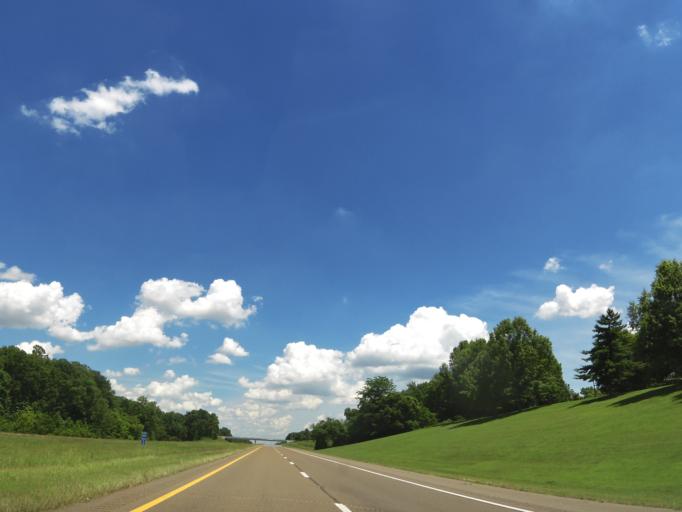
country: US
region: Tennessee
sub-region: Dyer County
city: Dyersburg
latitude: 36.0724
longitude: -89.4713
